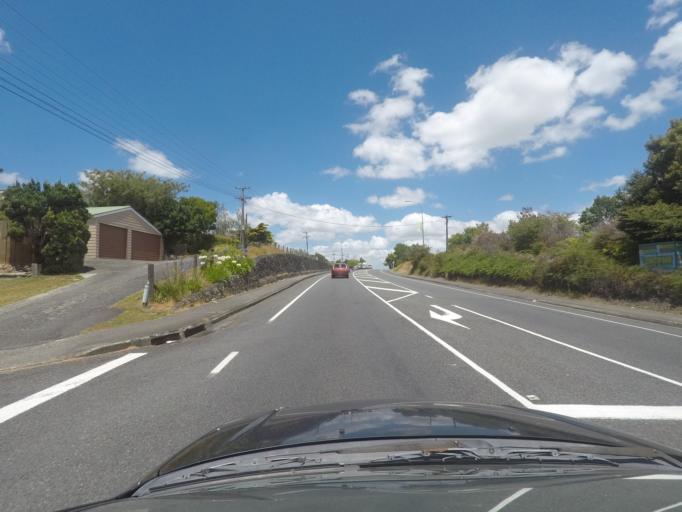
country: NZ
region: Northland
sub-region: Whangarei
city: Whangarei
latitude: -35.7461
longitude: 174.3671
